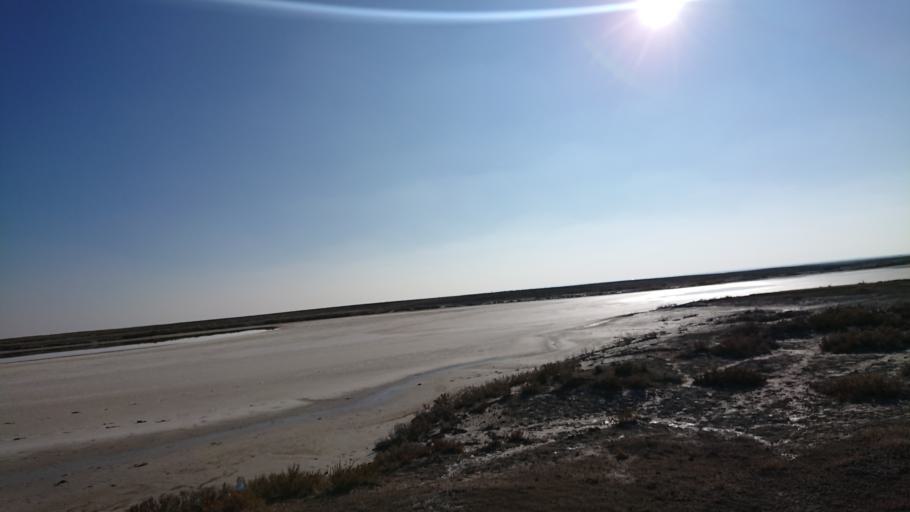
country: TR
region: Aksaray
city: Eskil
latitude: 38.4286
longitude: 33.5067
